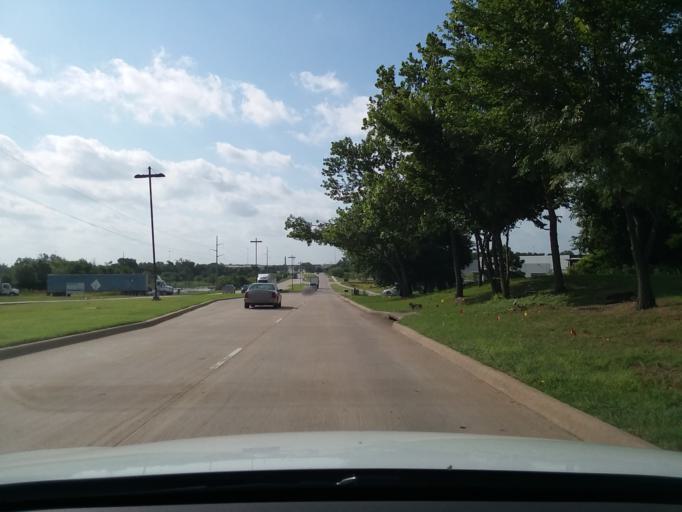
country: US
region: Texas
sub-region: Dallas County
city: Coppell
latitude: 32.9885
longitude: -97.0318
